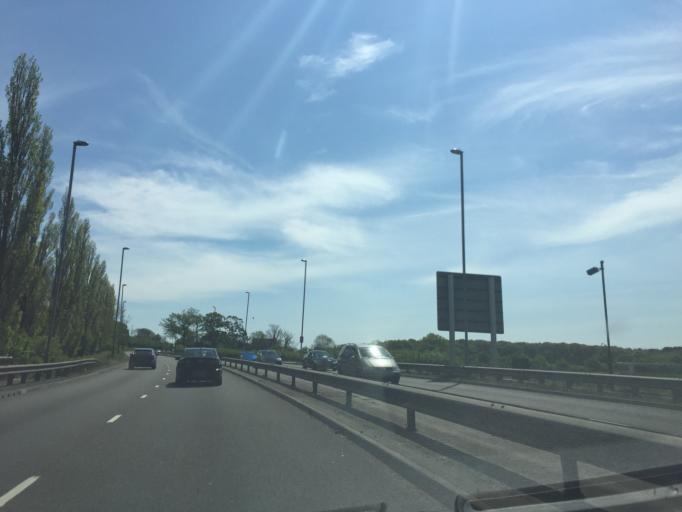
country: GB
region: England
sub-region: Essex
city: Harlow
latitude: 51.7549
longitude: 0.1286
